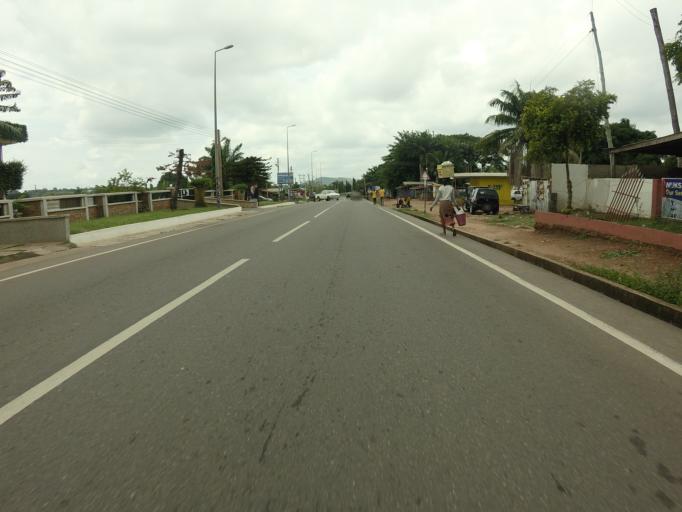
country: GH
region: Volta
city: Ho
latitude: 6.6080
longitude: 0.4773
